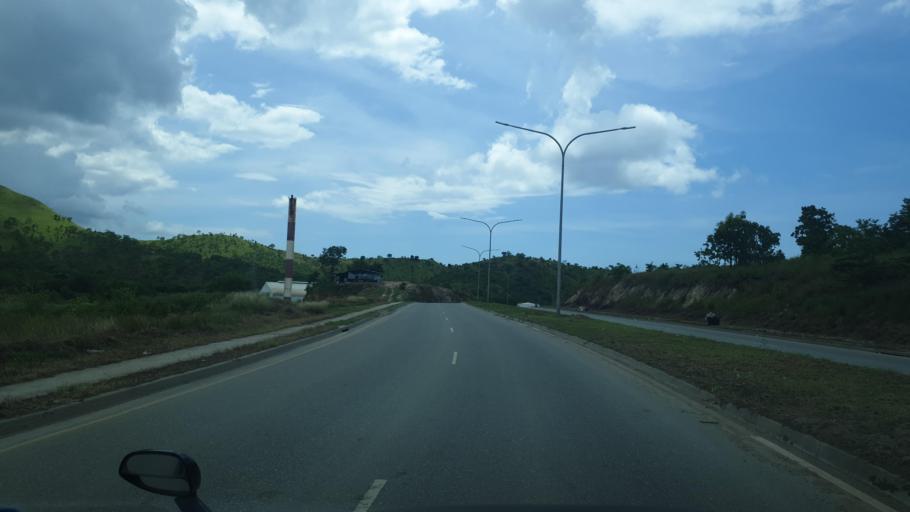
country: PG
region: National Capital
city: Port Moresby
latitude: -9.4287
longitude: 147.1408
